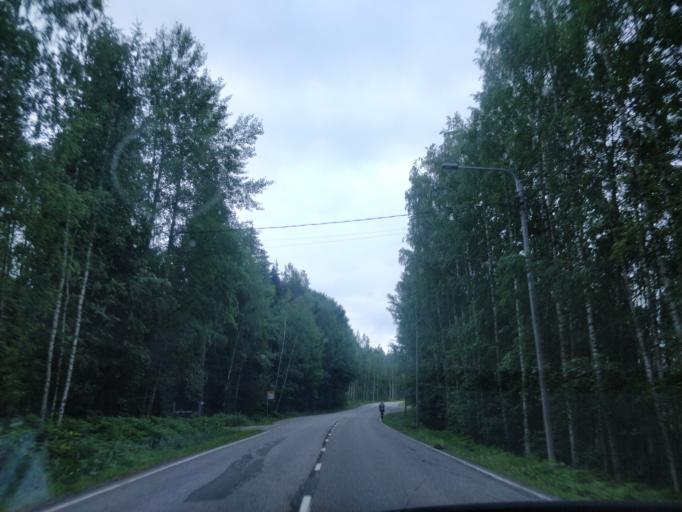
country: FI
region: Uusimaa
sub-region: Helsinki
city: Kauniainen
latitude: 60.2814
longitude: 24.7100
